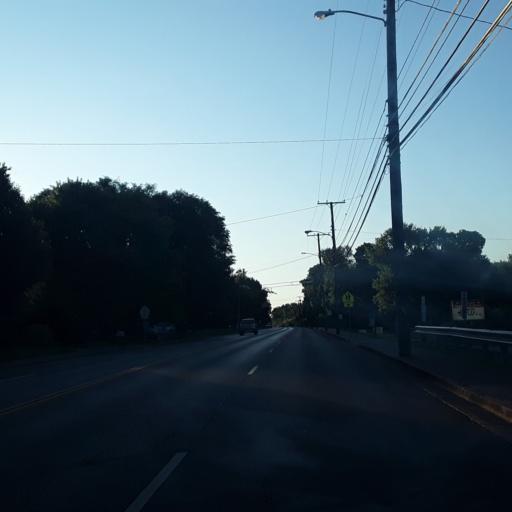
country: US
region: Tennessee
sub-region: Davidson County
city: Oak Hill
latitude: 36.1011
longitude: -86.7350
